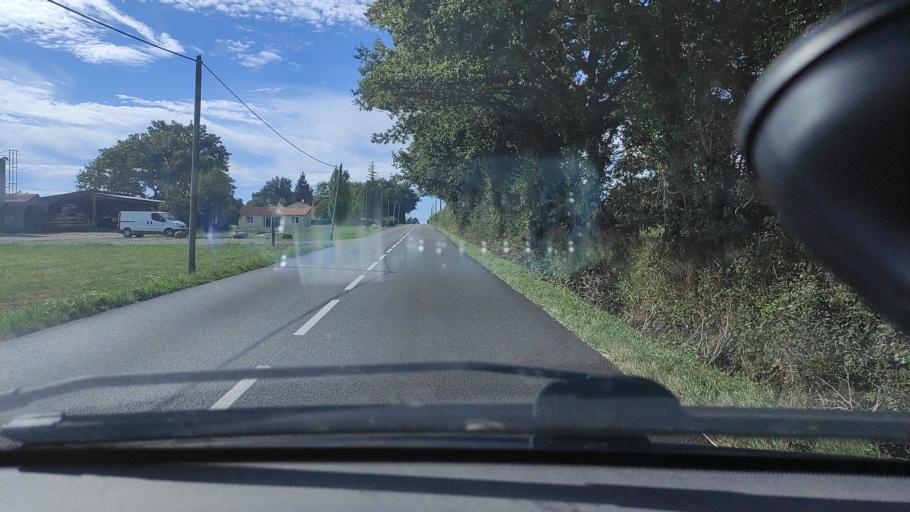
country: FR
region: Pays de la Loire
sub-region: Departement de la Vendee
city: La Boissiere-des-Landes
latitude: 46.5539
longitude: -1.4312
